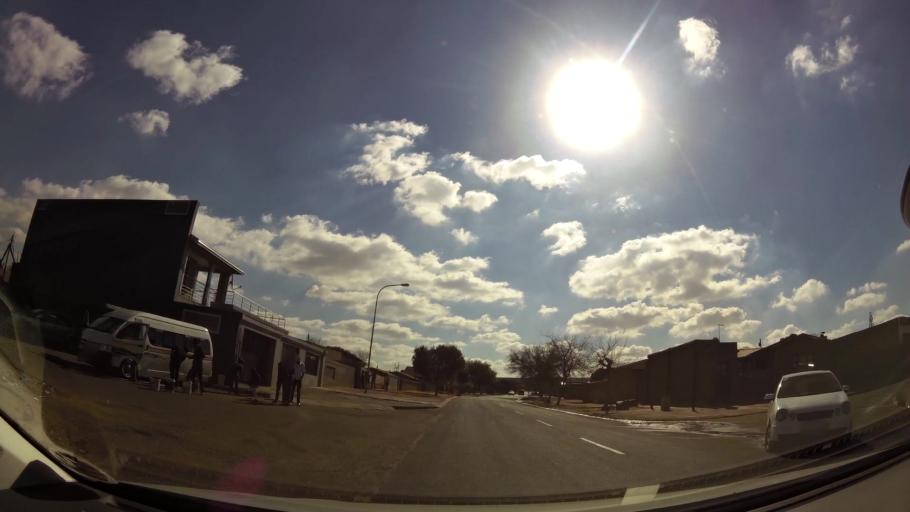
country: ZA
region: Gauteng
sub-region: City of Johannesburg Metropolitan Municipality
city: Roodepoort
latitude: -26.2097
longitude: 27.8801
